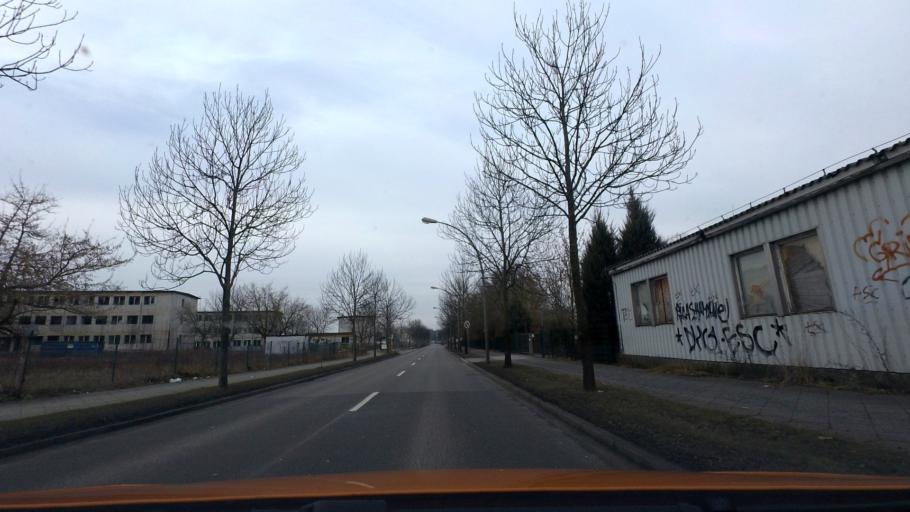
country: DE
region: Berlin
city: Blankenburg
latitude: 52.5872
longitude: 13.4573
